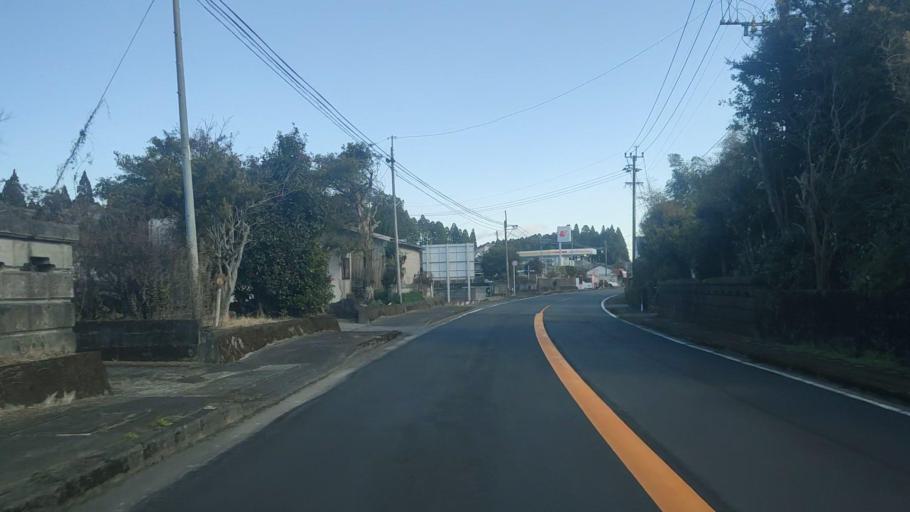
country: JP
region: Kagoshima
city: Sueyoshicho-ninokata
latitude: 31.6834
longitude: 130.9404
